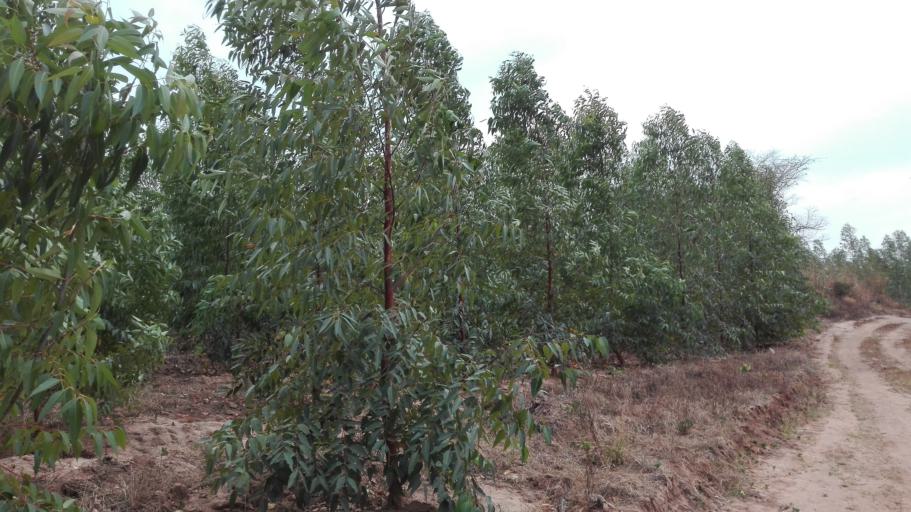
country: MZ
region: Nampula
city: Mutuali
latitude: -15.6616
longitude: 36.9208
